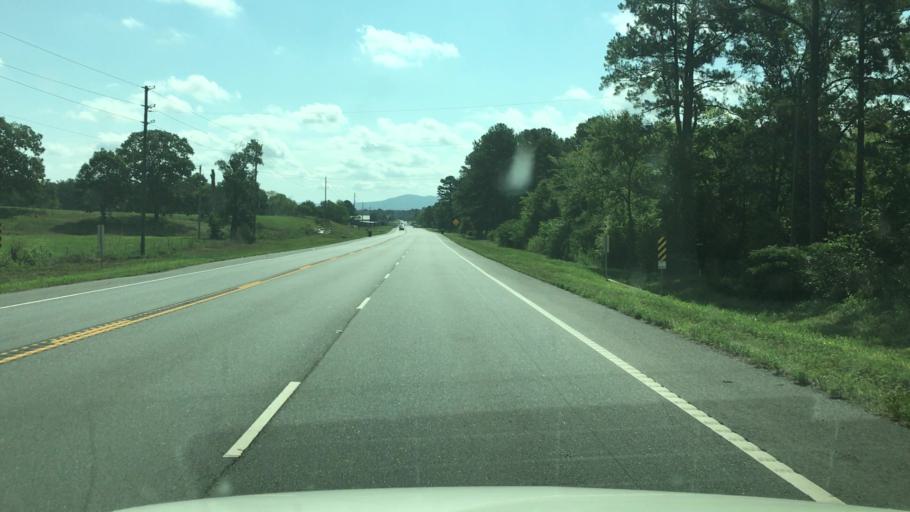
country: US
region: Arkansas
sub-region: Garland County
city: Piney
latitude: 34.5109
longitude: -93.2294
